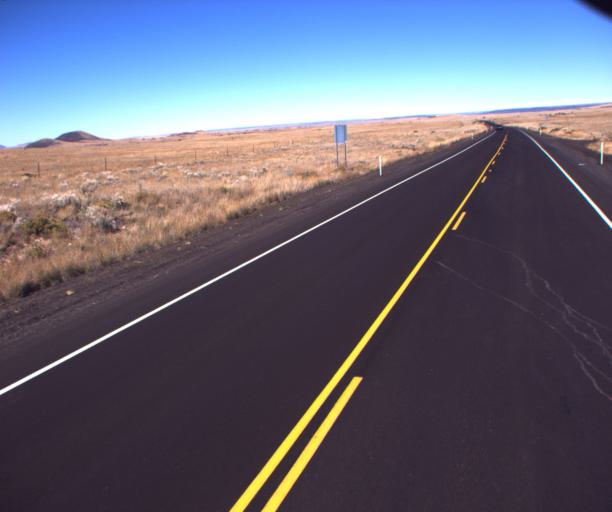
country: US
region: Arizona
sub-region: Apache County
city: Springerville
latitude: 34.1834
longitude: -109.3191
